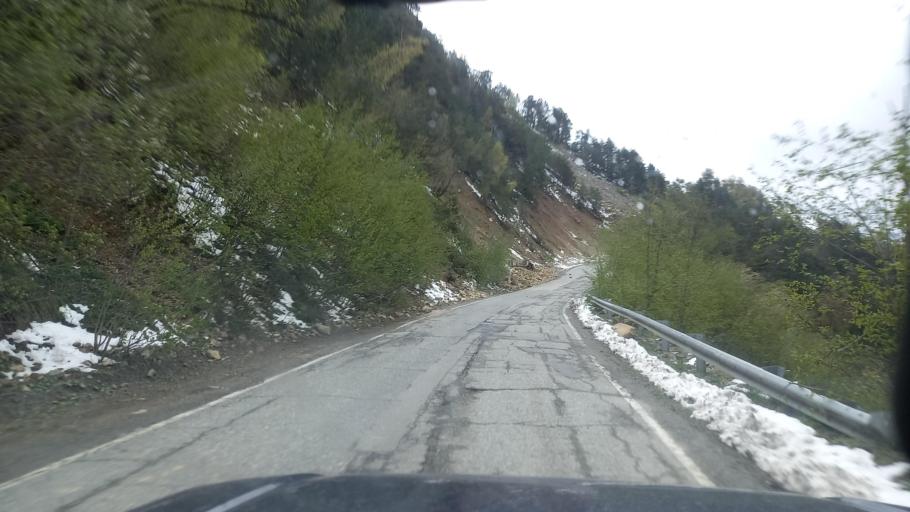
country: RU
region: North Ossetia
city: Mizur
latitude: 42.7982
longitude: 43.9265
